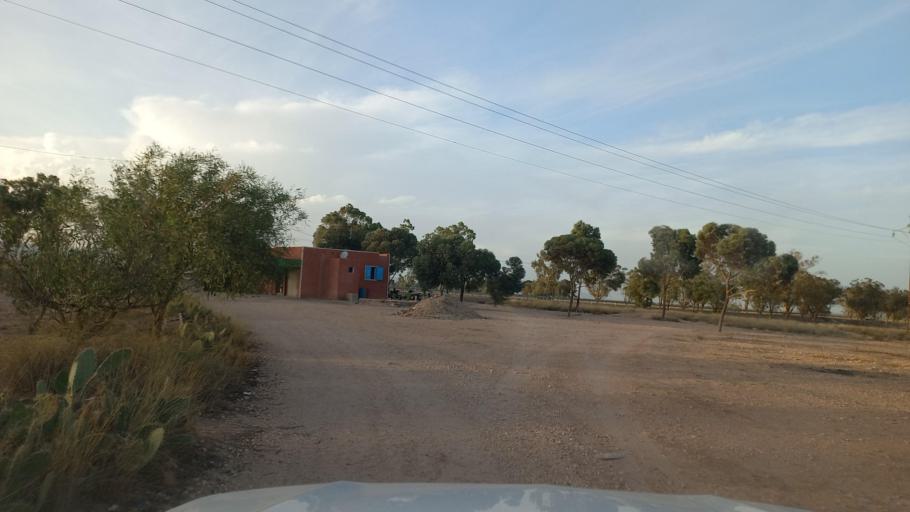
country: TN
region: Al Qasrayn
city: Kasserine
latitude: 35.2421
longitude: 8.9917
